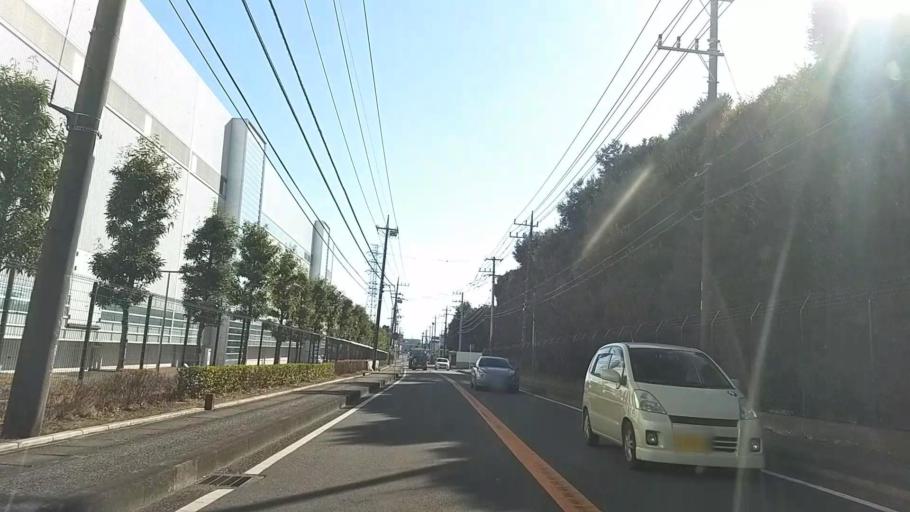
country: JP
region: Kanagawa
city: Hadano
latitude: 35.3874
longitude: 139.2080
